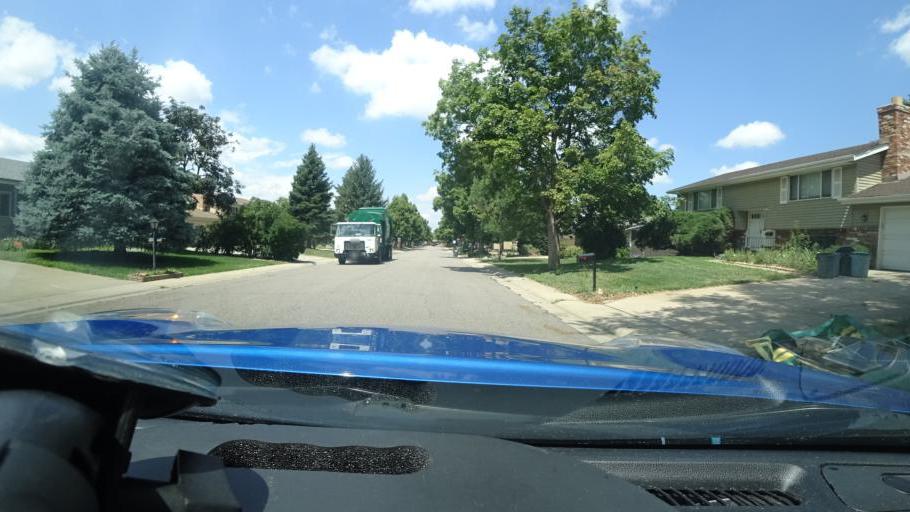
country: US
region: Colorado
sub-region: Adams County
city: Aurora
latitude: 39.7063
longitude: -104.8424
